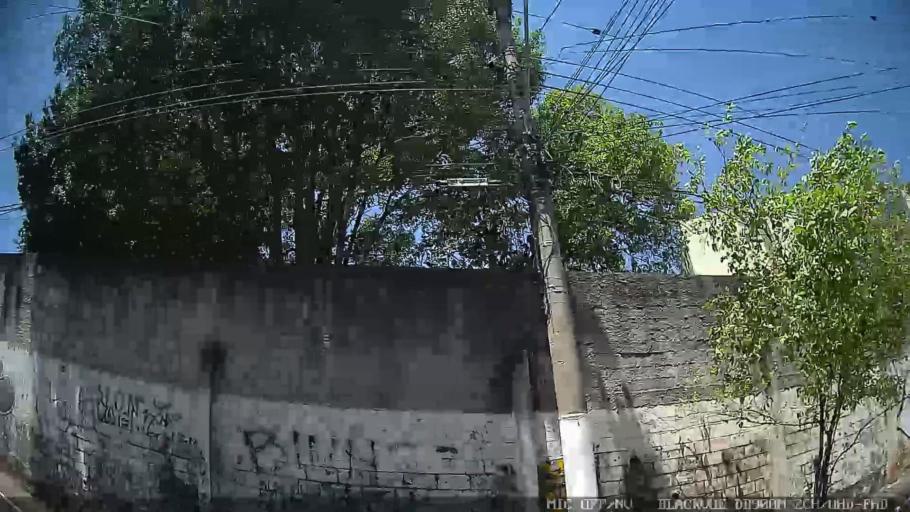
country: BR
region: Sao Paulo
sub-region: Sao Caetano Do Sul
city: Sao Caetano do Sul
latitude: -23.6018
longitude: -46.5501
